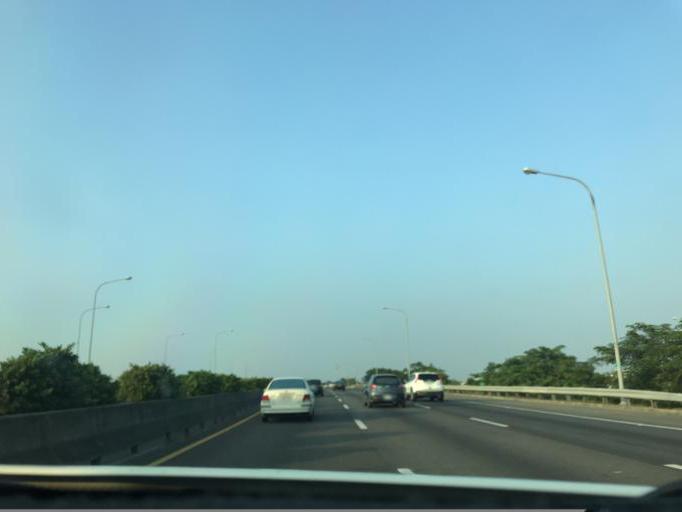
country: TW
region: Taiwan
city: Xinying
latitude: 23.1804
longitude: 120.2354
